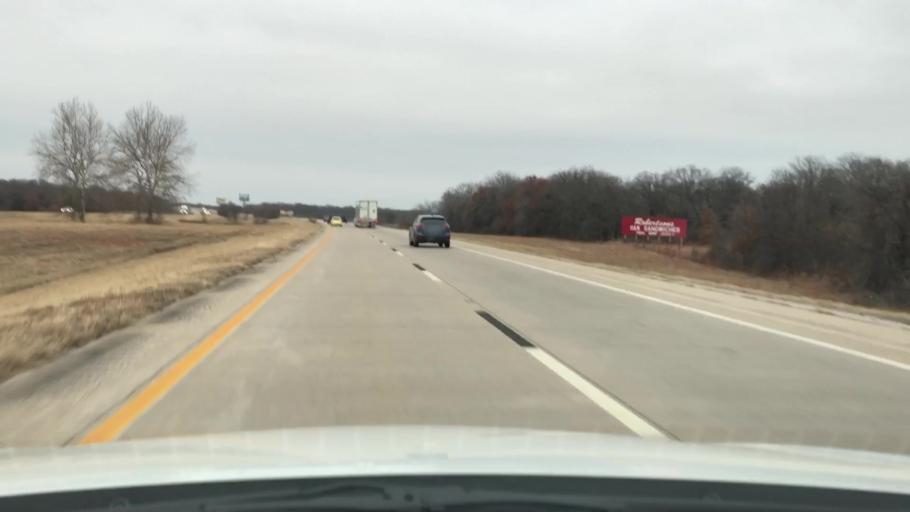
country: US
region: Oklahoma
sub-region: Love County
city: Marietta
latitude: 33.8221
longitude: -97.1301
